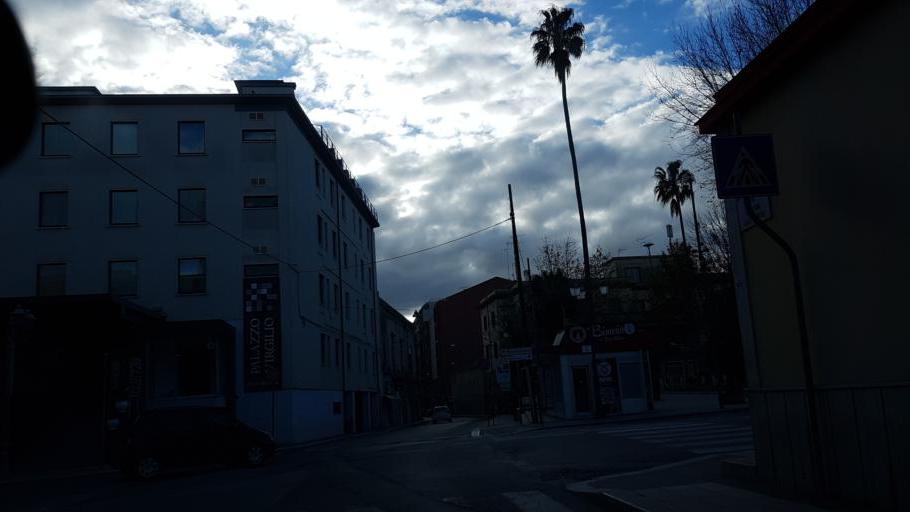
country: IT
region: Apulia
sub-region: Provincia di Brindisi
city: Brindisi
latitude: 40.6348
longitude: 17.9399
